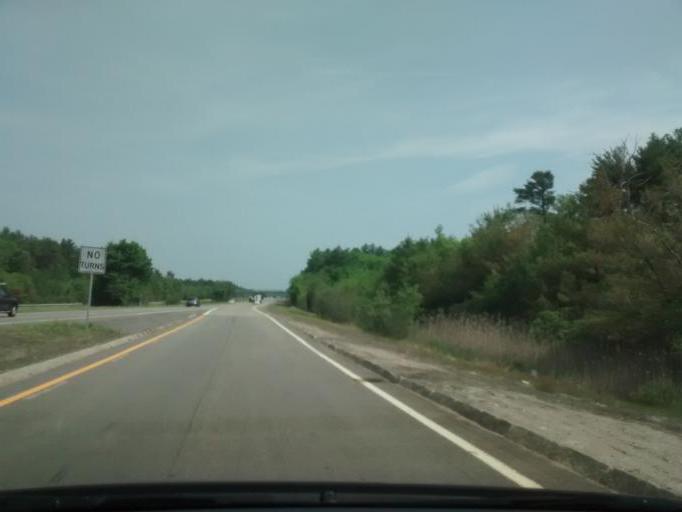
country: US
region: Massachusetts
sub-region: Bristol County
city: Norton Center
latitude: 41.9796
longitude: -71.1572
